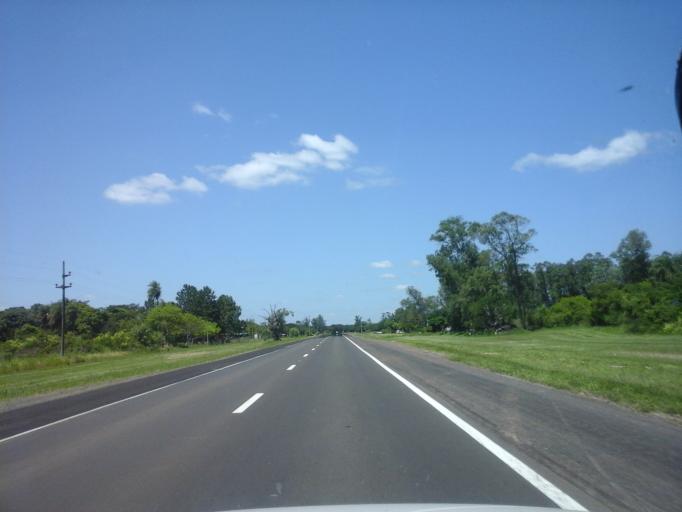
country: AR
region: Corrientes
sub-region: Departamento de Itati
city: Itati
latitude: -27.3616
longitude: -58.2689
